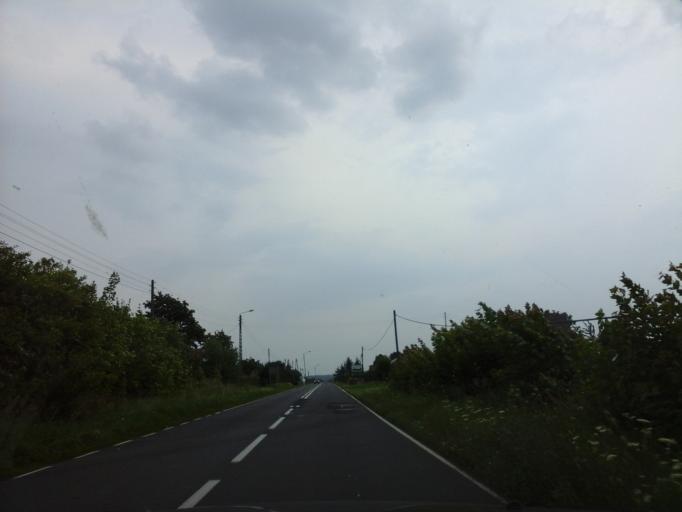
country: PL
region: Lubusz
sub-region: Powiat strzelecko-drezdenecki
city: Dobiegniew
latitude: 52.9444
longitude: 15.7511
